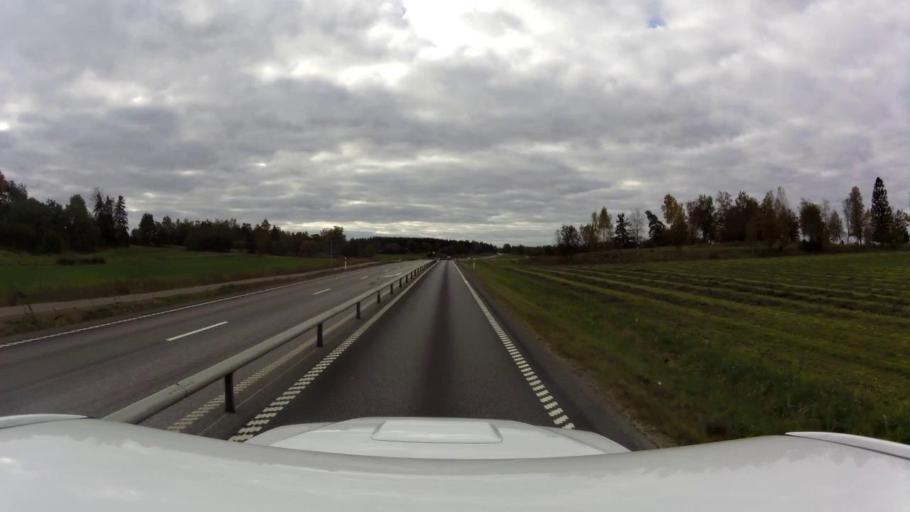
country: SE
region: OEstergoetland
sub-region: Linkopings Kommun
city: Malmslatt
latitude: 58.3122
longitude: 15.5671
